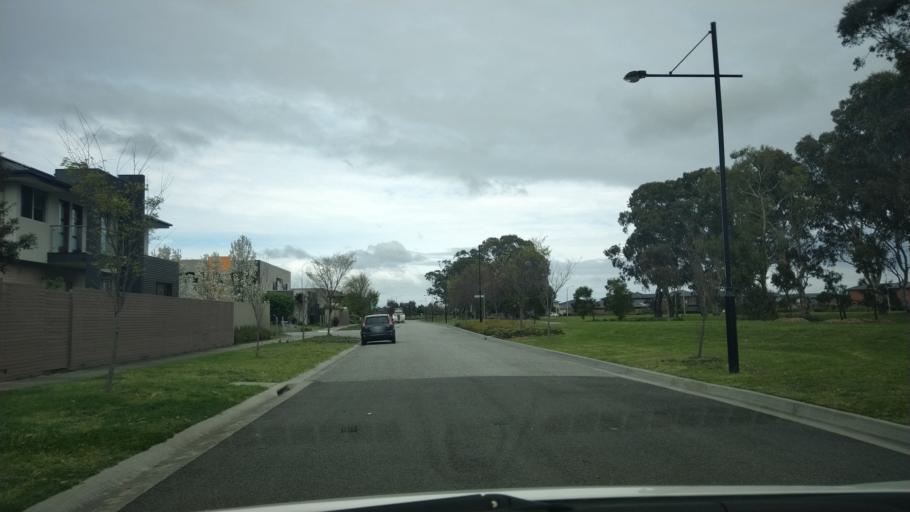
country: AU
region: Victoria
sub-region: Greater Dandenong
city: Keysborough
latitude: -38.0069
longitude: 145.1750
